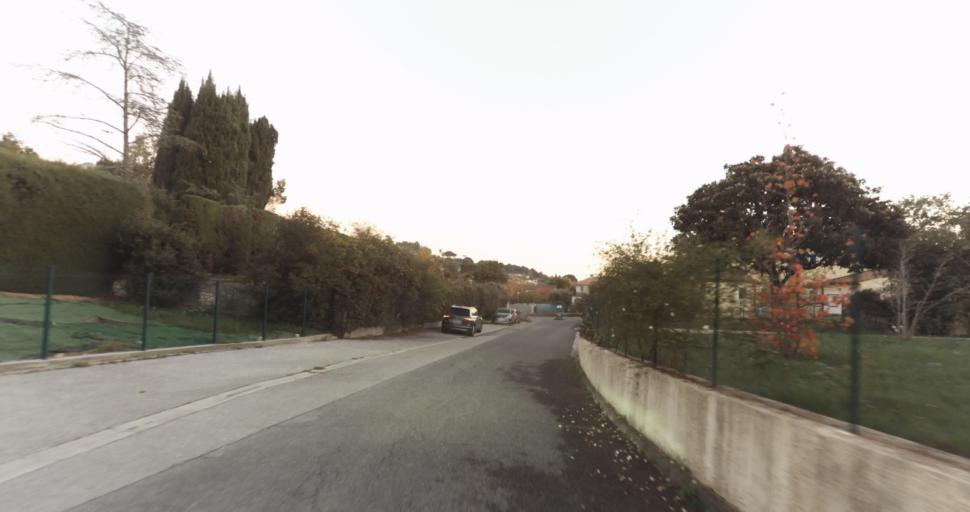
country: FR
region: Provence-Alpes-Cote d'Azur
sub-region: Departement des Alpes-Maritimes
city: Vence
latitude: 43.7162
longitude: 7.1279
